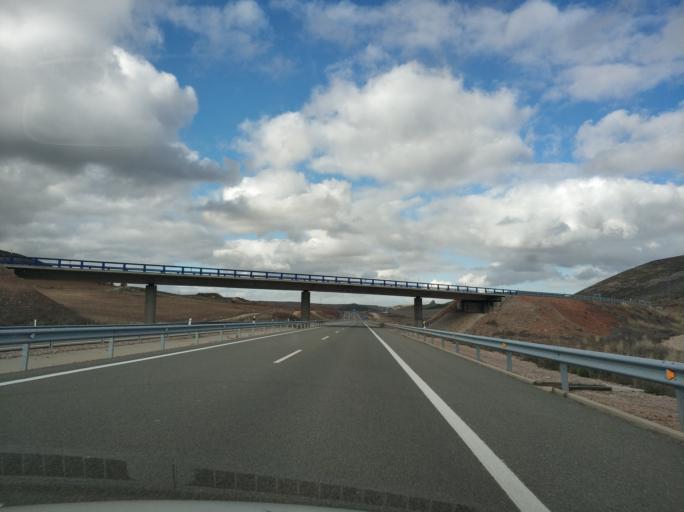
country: ES
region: Castille and Leon
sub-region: Provincia de Soria
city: Medinaceli
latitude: 41.1999
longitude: -2.4596
